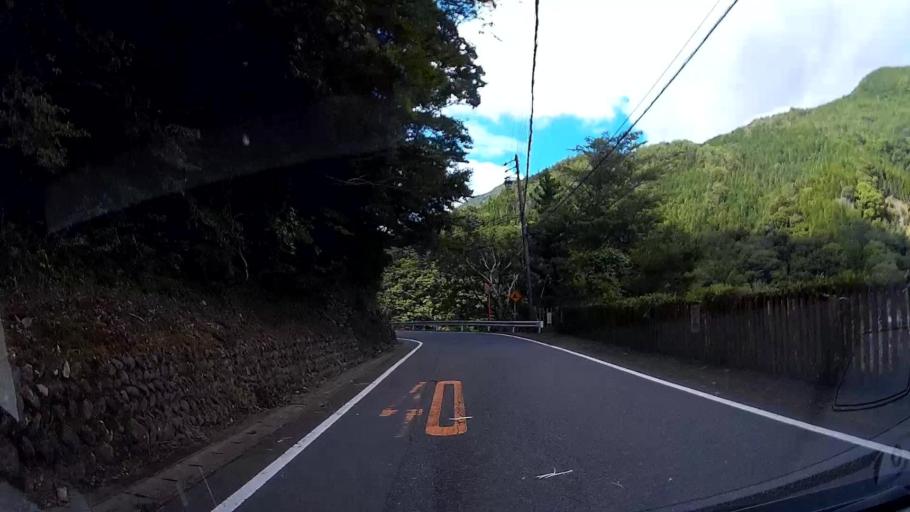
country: JP
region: Shizuoka
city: Shizuoka-shi
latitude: 35.2564
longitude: 138.2398
